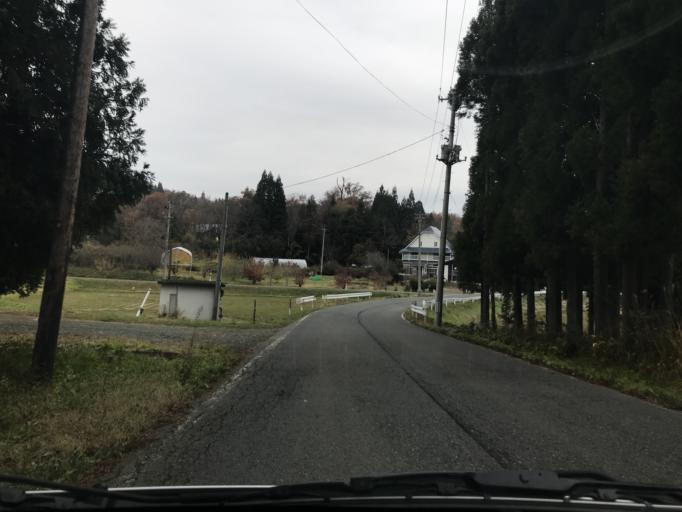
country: JP
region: Iwate
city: Kitakami
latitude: 39.2873
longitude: 141.1749
